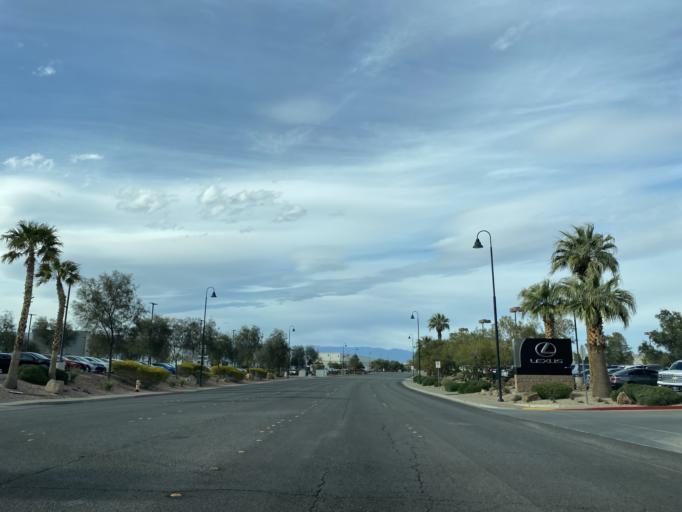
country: US
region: Nevada
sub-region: Clark County
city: Henderson
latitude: 36.0477
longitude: -115.0195
